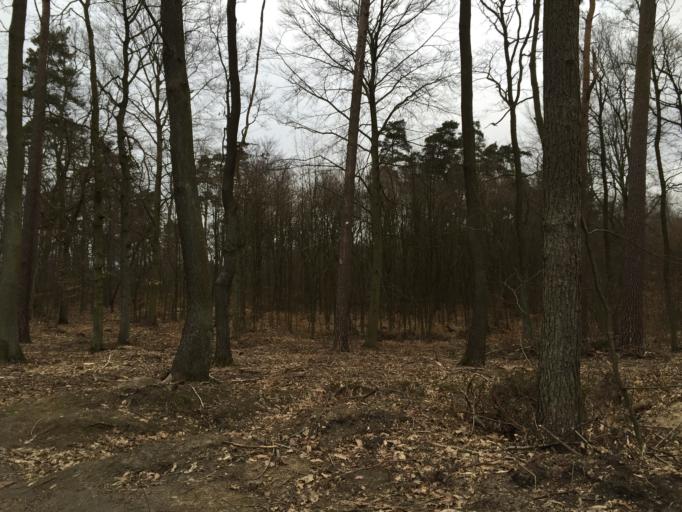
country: PL
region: Pomeranian Voivodeship
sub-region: Sopot
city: Sopot
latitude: 54.3802
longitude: 18.5221
